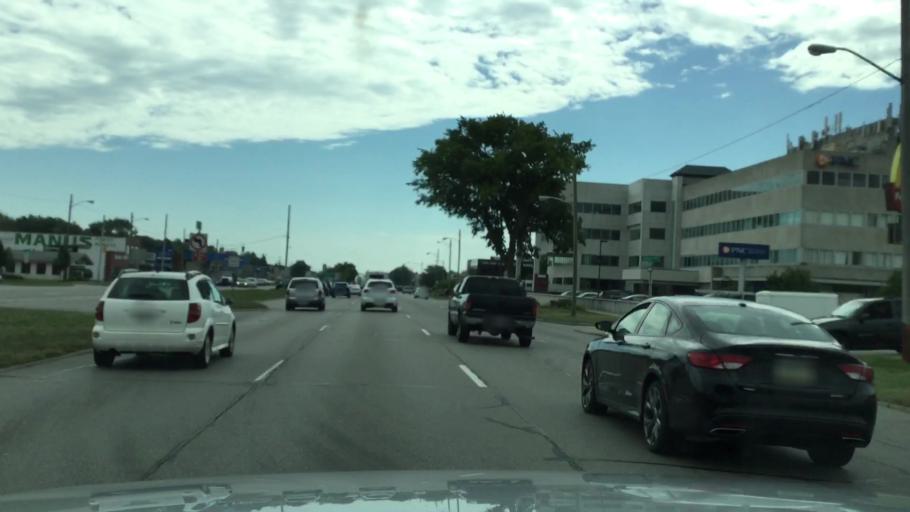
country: US
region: Michigan
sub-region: Oakland County
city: Berkley
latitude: 42.5160
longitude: -83.1846
